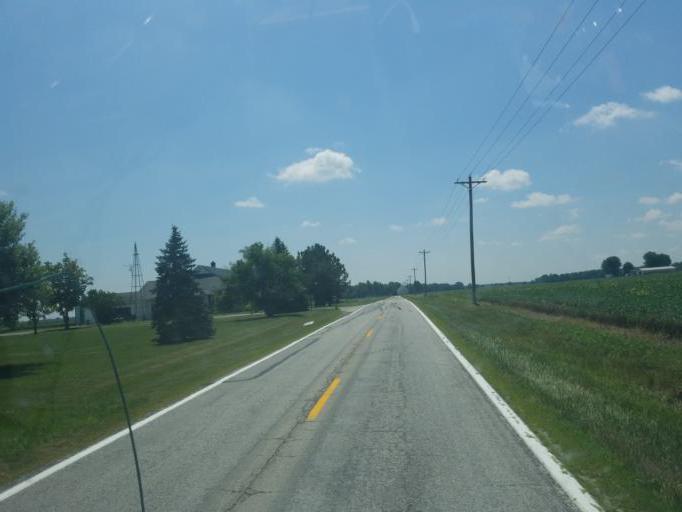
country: US
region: Ohio
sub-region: Allen County
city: Spencerville
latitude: 40.6814
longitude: -84.4256
